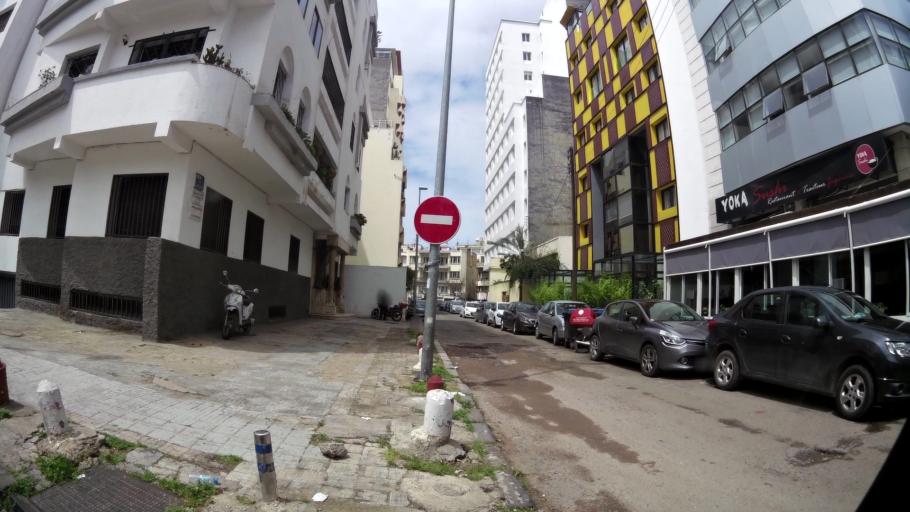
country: MA
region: Grand Casablanca
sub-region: Casablanca
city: Casablanca
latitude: 33.5924
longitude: -7.6313
